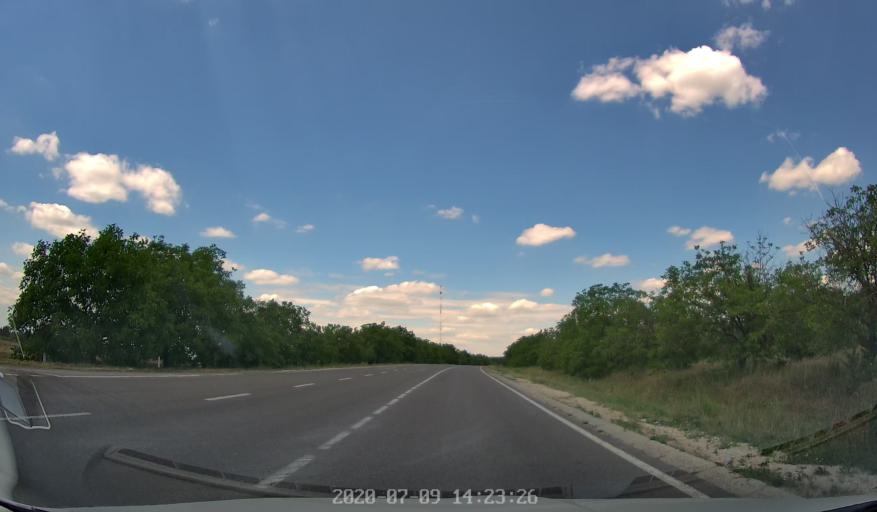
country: MD
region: Rezina
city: Saharna
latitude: 47.6541
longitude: 28.8277
